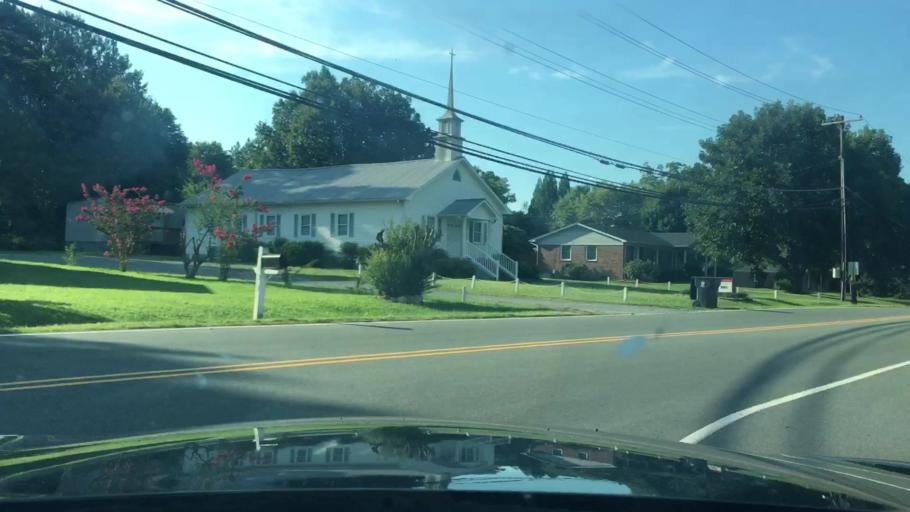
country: US
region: North Carolina
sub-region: Alamance County
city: Elon
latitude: 36.0964
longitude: -79.5078
